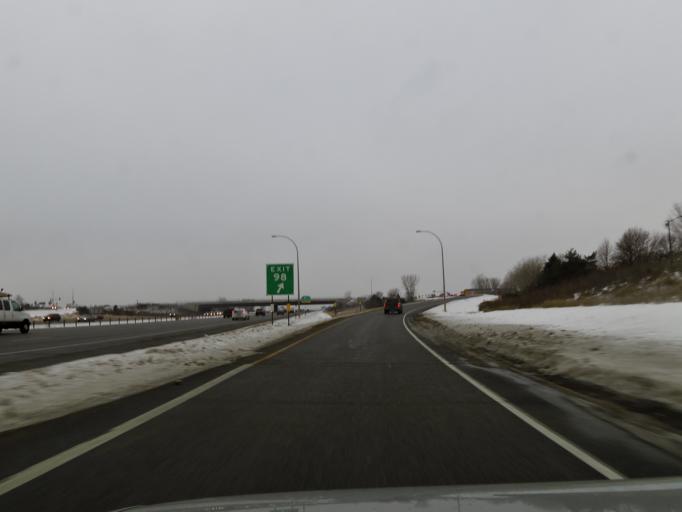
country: US
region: Minnesota
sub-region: Dakota County
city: Mendota Heights
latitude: 44.8512
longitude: -93.1510
